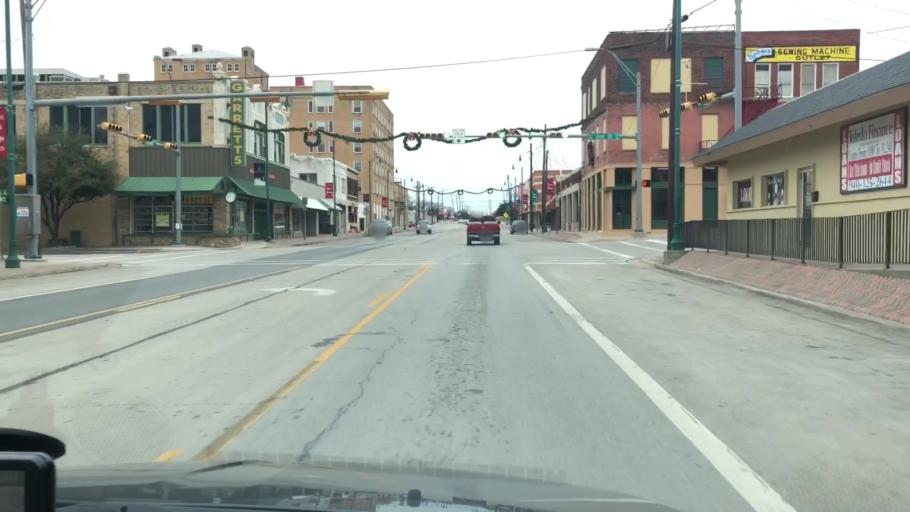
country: US
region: Texas
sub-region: Palo Pinto County
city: Mineral Wells
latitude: 32.8106
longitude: -98.1128
